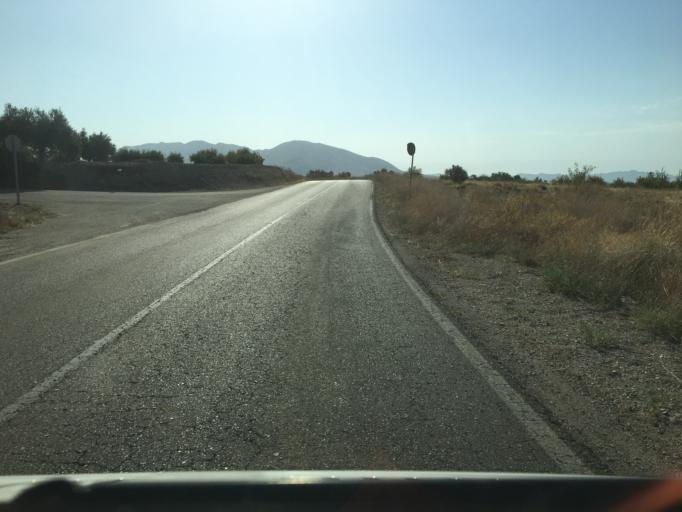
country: ES
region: Andalusia
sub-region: Provincia de Almeria
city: Huercal-Overa
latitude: 37.4700
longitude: -1.9062
